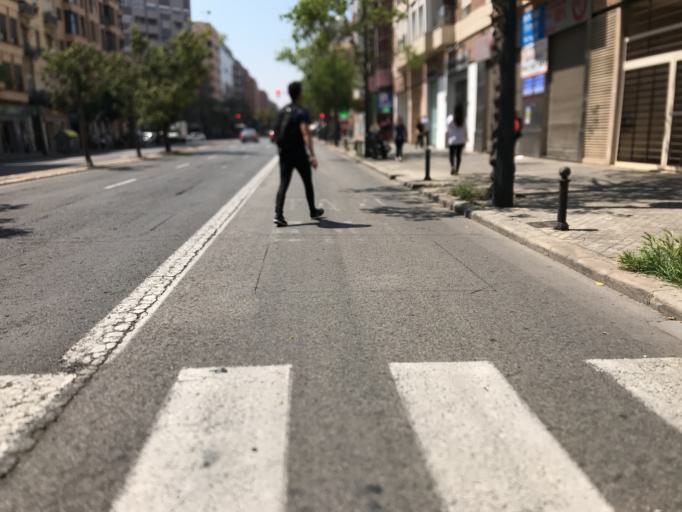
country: ES
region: Valencia
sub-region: Provincia de Valencia
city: Valencia
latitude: 39.4703
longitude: -0.3551
